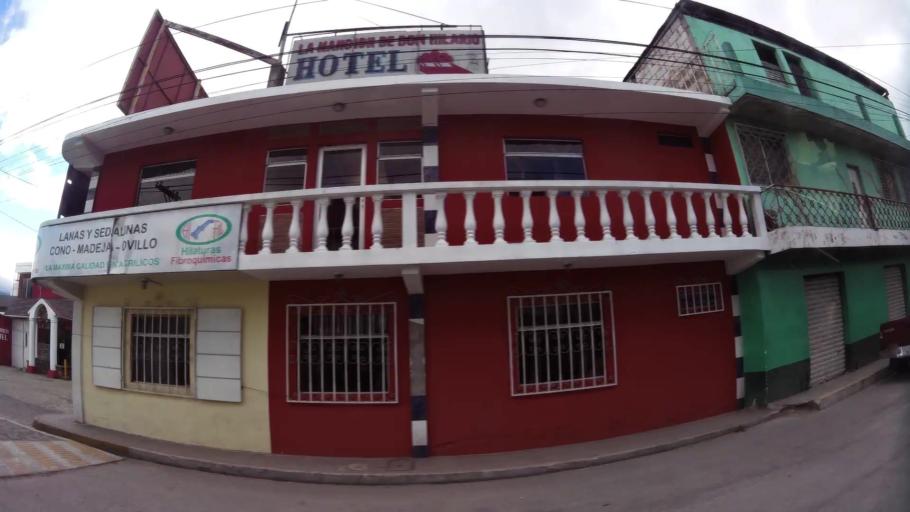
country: GT
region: Quetzaltenango
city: Salcaja
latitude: 14.8771
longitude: -91.4610
